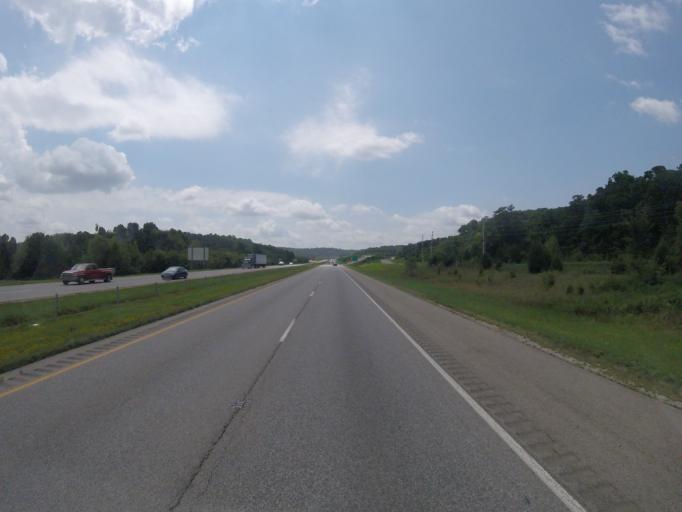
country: US
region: Arkansas
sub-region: Washington County
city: Fayetteville
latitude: 36.0455
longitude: -94.1910
